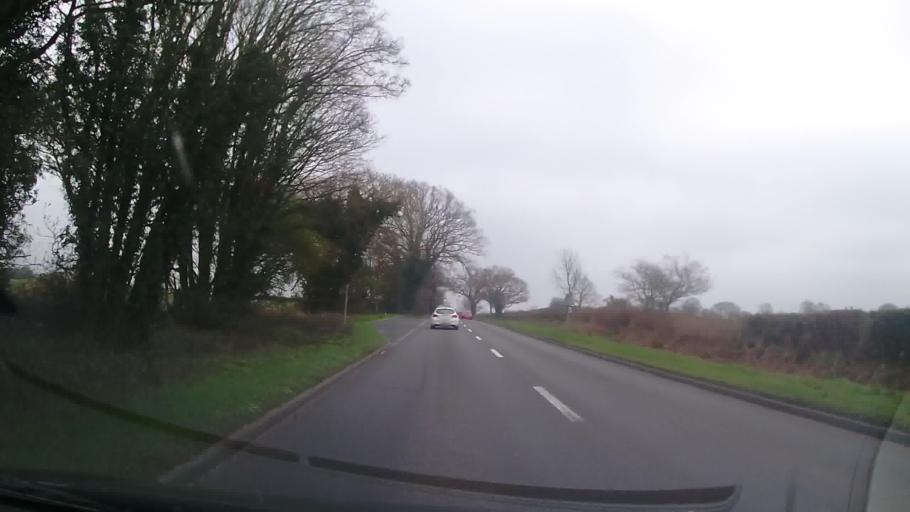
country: GB
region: England
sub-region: Shropshire
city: Market Drayton
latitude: 52.9137
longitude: -2.4377
